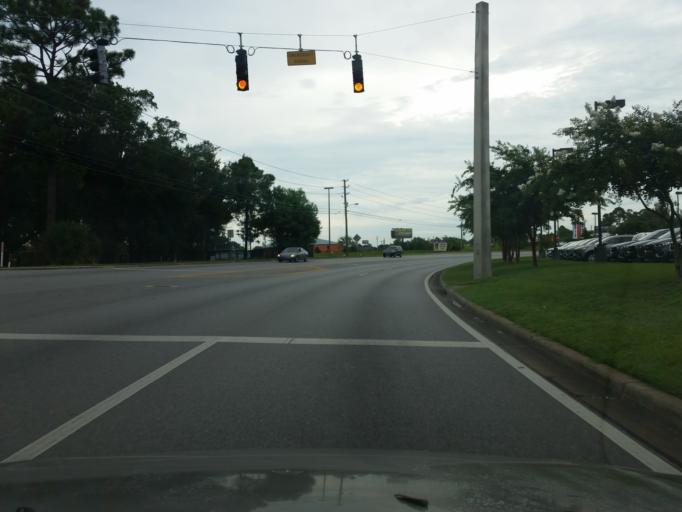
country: US
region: Florida
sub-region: Escambia County
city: Brent
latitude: 30.4839
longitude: -87.2602
